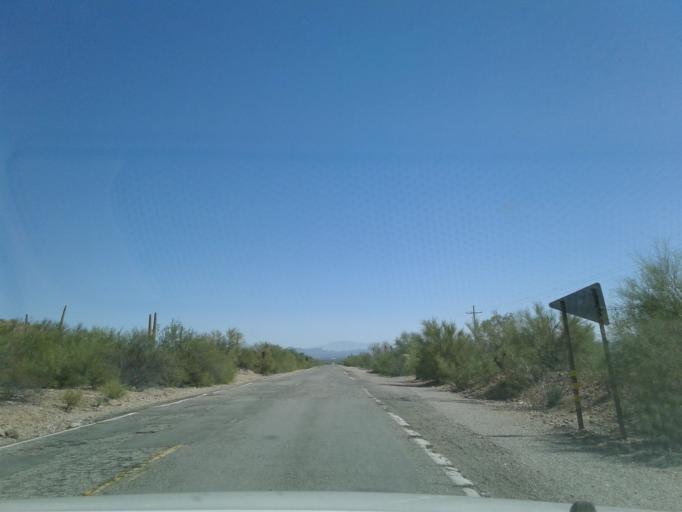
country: US
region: Arizona
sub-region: Pima County
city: Avra Valley
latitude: 32.3781
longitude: -111.4839
